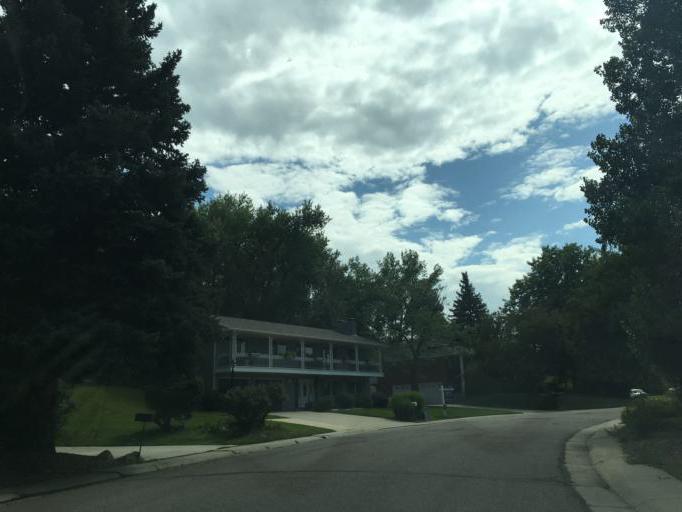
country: US
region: Colorado
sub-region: Jefferson County
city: Applewood
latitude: 39.7487
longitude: -105.1305
